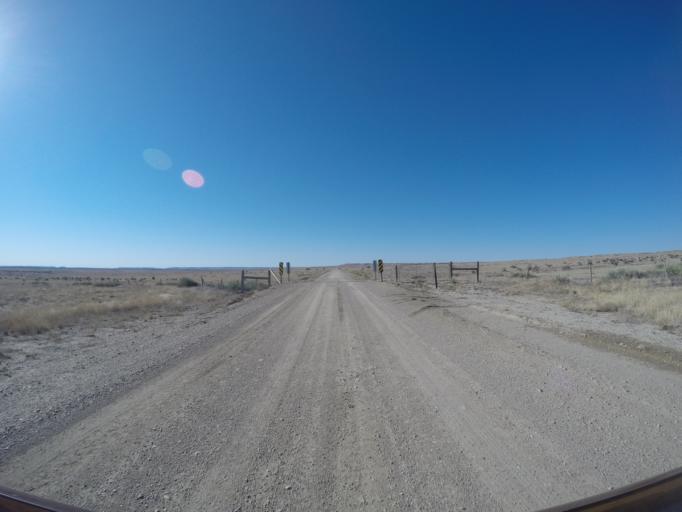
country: US
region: Colorado
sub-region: Otero County
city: La Junta
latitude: 37.7833
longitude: -103.5371
